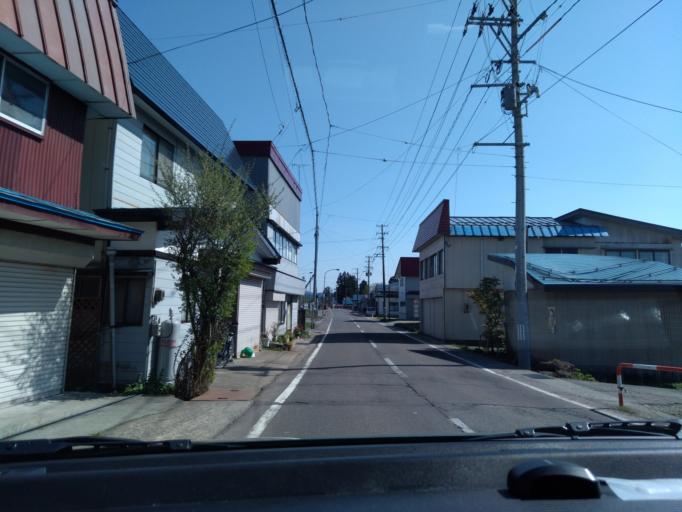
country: JP
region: Akita
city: Kakunodatemachi
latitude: 39.4965
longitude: 140.5940
